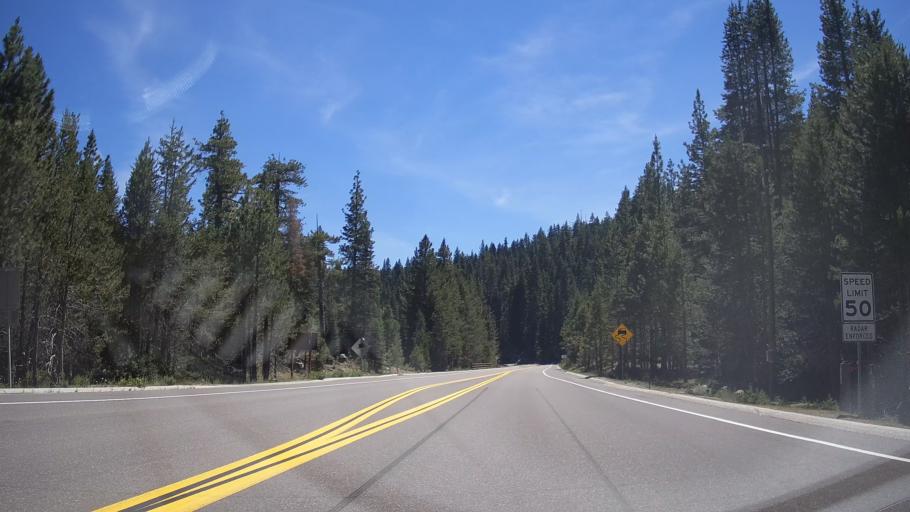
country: US
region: California
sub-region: Placer County
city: Sunnyside-Tahoe City
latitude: 39.2035
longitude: -120.2002
